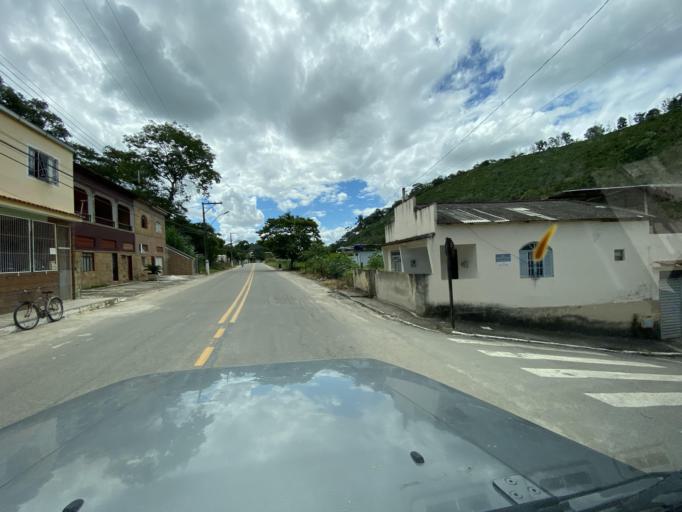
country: BR
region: Espirito Santo
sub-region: Jeronimo Monteiro
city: Jeronimo Monteiro
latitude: -20.7912
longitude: -41.3826
